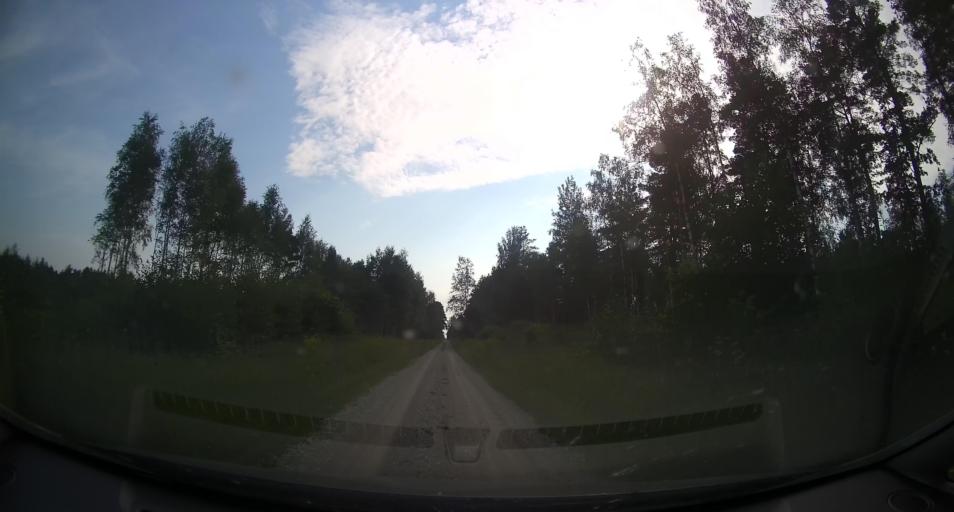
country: EE
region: Laeaene
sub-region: Lihula vald
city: Lihula
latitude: 58.6484
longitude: 23.7868
